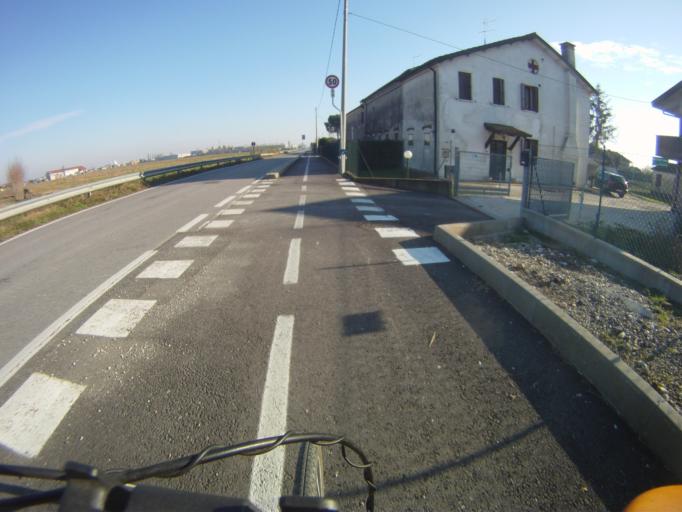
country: IT
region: Veneto
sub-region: Provincia di Padova
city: Brugine
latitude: 45.3104
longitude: 11.9843
